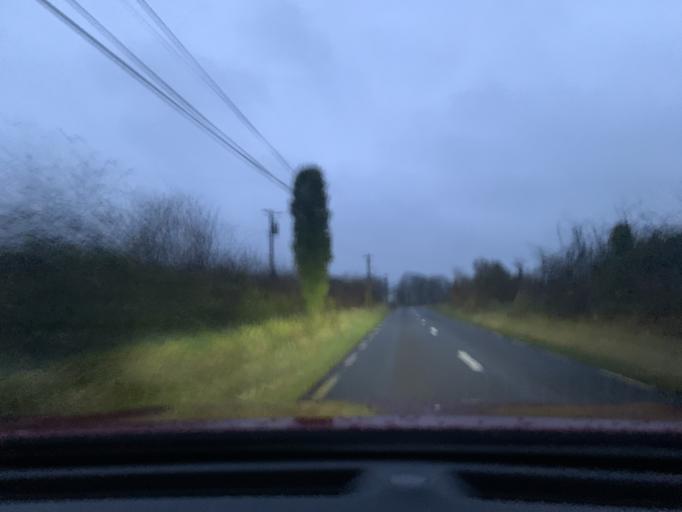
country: IE
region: Connaught
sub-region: Sligo
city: Ballymote
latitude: 54.0525
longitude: -8.5228
